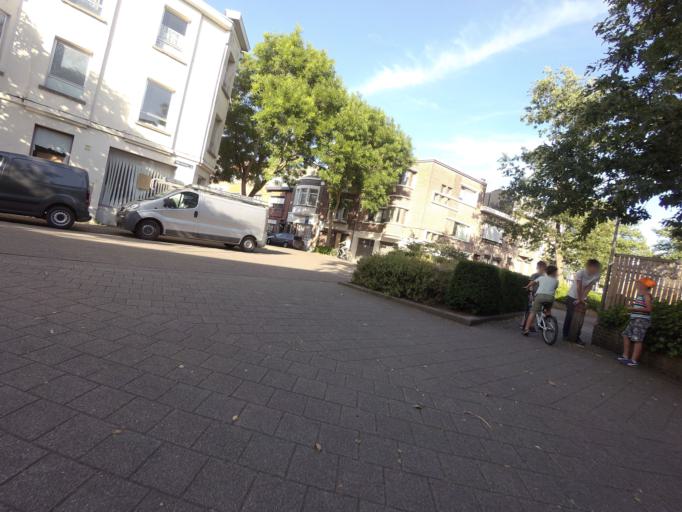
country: BE
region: Flanders
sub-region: Provincie Antwerpen
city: Mortsel
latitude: 51.1703
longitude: 4.4444
